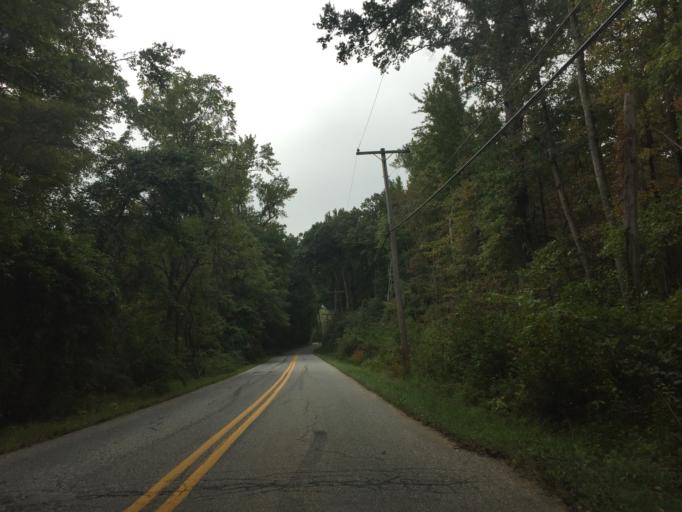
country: US
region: Maryland
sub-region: Baltimore County
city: Bowleys Quarters
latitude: 39.3659
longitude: -76.3886
